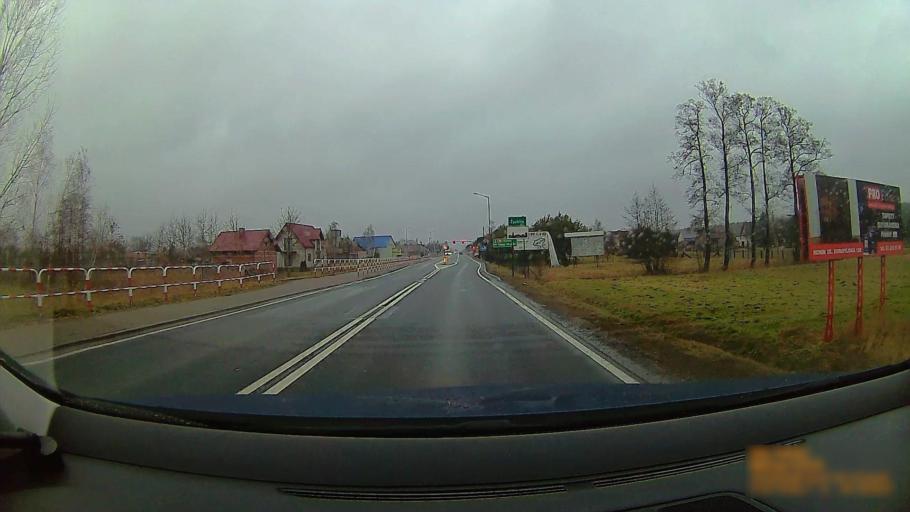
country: PL
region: Greater Poland Voivodeship
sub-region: Konin
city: Konin
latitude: 52.1745
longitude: 18.2723
